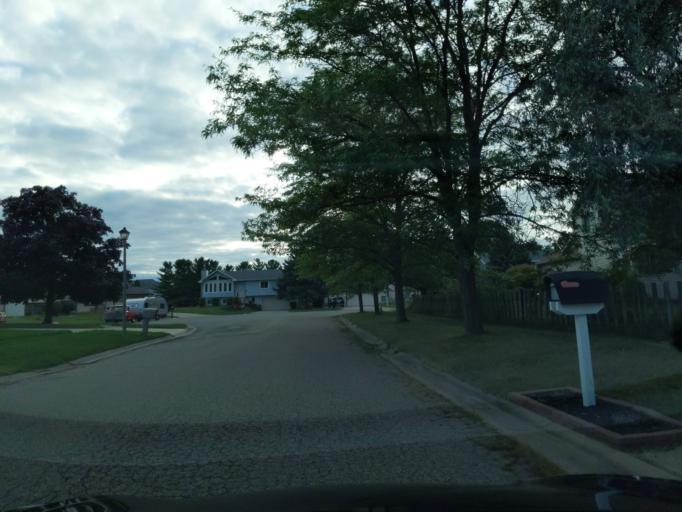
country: US
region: Michigan
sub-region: Eaton County
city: Waverly
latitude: 42.7233
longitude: -84.6211
